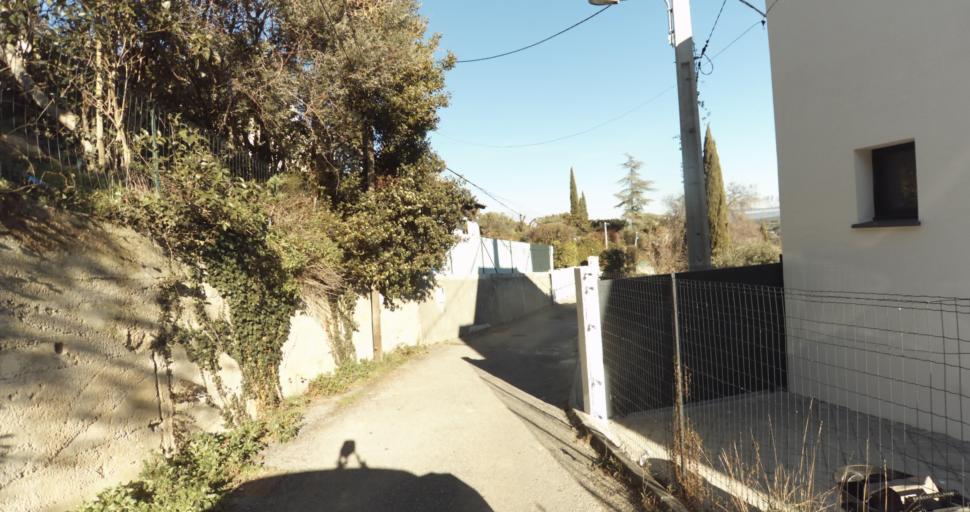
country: FR
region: Provence-Alpes-Cote d'Azur
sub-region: Departement des Bouches-du-Rhone
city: Cadolive
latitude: 43.3907
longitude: 5.5473
